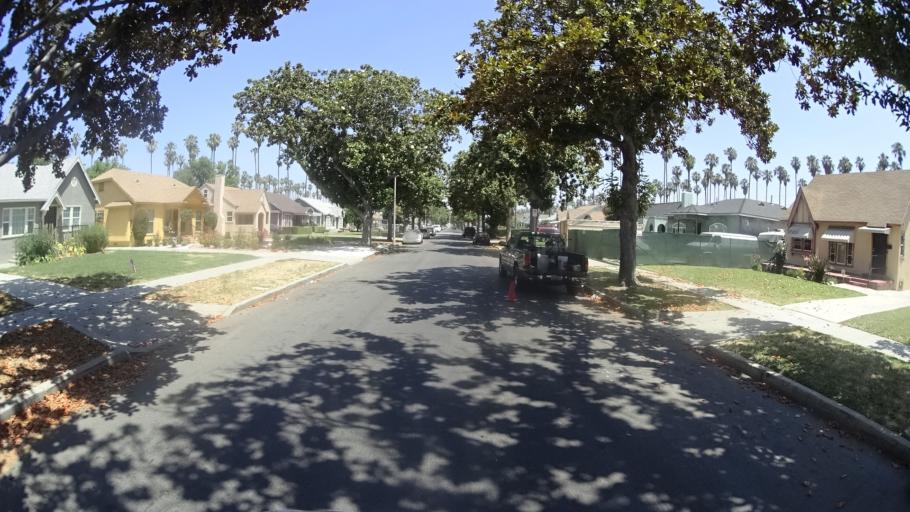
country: US
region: California
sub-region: Los Angeles County
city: View Park-Windsor Hills
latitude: 33.9968
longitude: -118.3247
